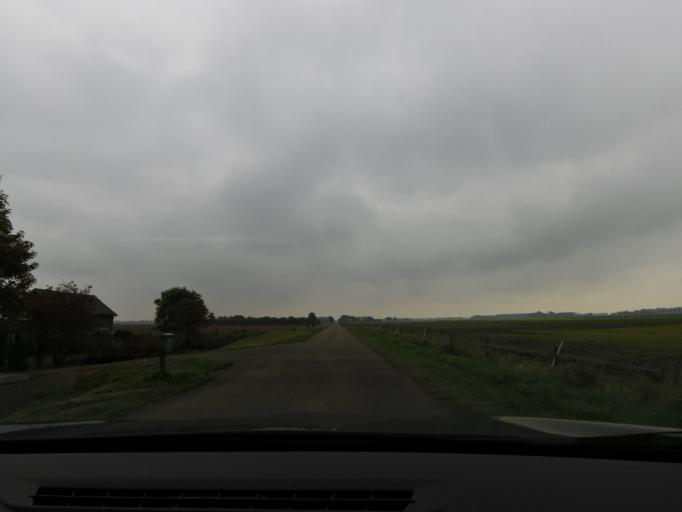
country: NL
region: South Holland
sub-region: Gemeente Goeree-Overflakkee
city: Dirksland
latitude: 51.7763
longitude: 4.0834
